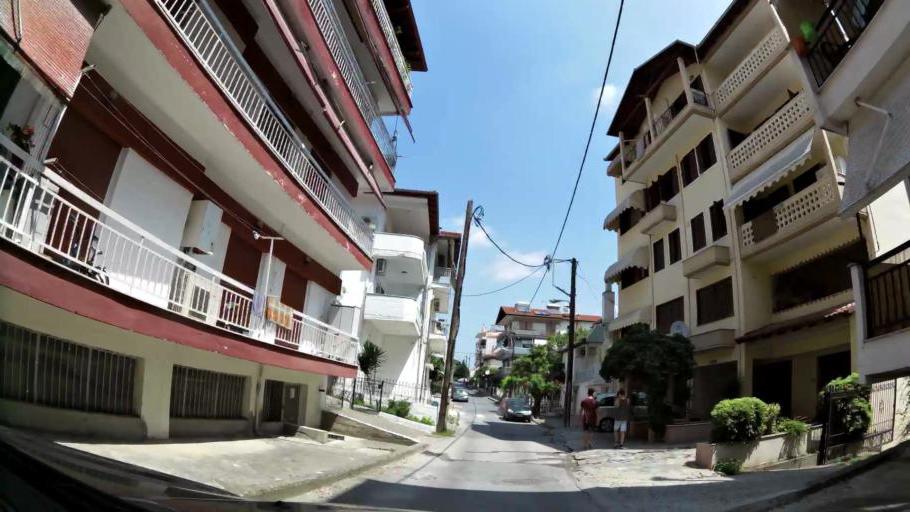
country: GR
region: Central Macedonia
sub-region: Nomos Imathias
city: Veroia
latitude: 40.5172
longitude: 22.2055
